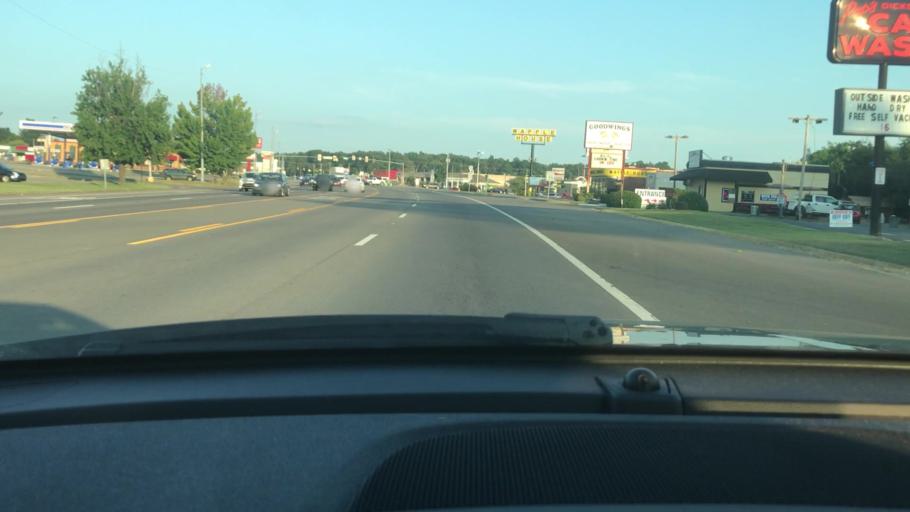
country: US
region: Tennessee
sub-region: Dickson County
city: Dickson
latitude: 36.0783
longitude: -87.3769
